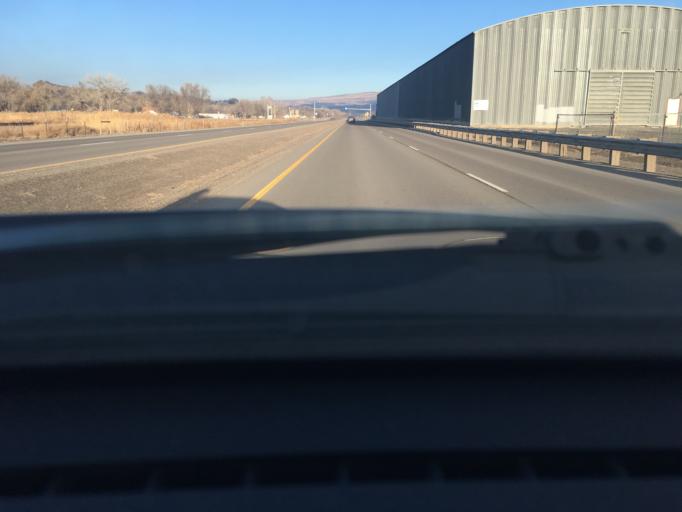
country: US
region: Colorado
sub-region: Delta County
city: Delta
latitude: 38.7333
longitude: -108.0738
